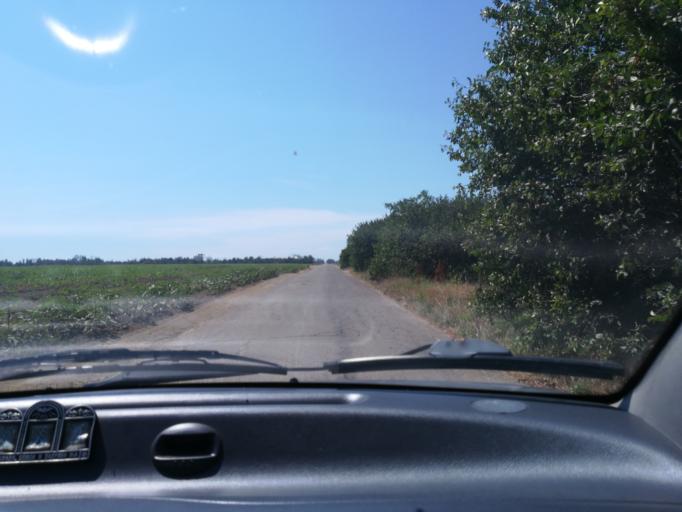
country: RU
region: Krasnodarskiy
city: Blagovetschenskaya
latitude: 45.0597
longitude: 37.0949
